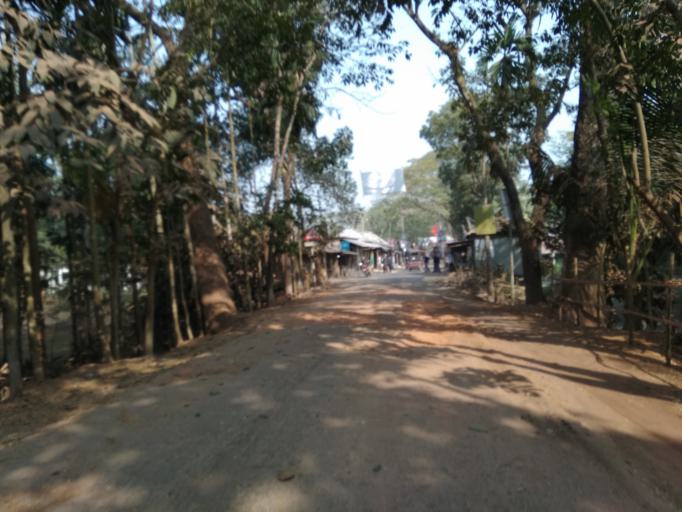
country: BD
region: Barisal
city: Mehendiganj
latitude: 22.9554
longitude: 90.4149
